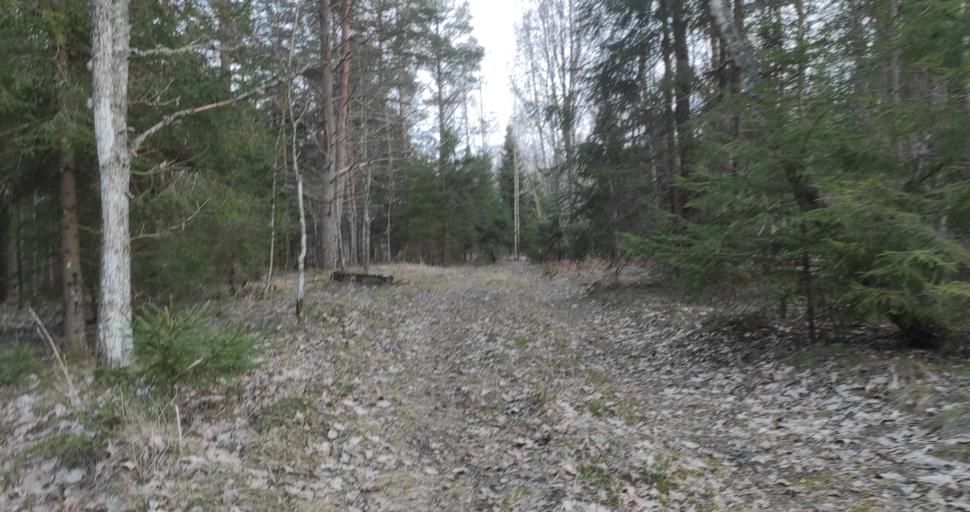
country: LV
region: Kuldigas Rajons
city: Kuldiga
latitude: 56.9114
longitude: 21.8907
